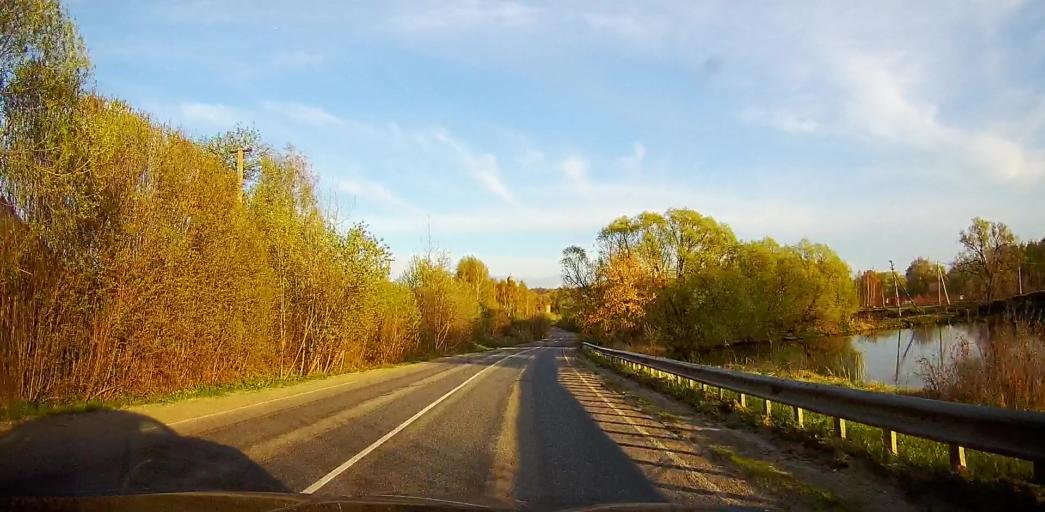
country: RU
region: Moskovskaya
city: Meshcherino
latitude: 55.2566
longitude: 38.2703
